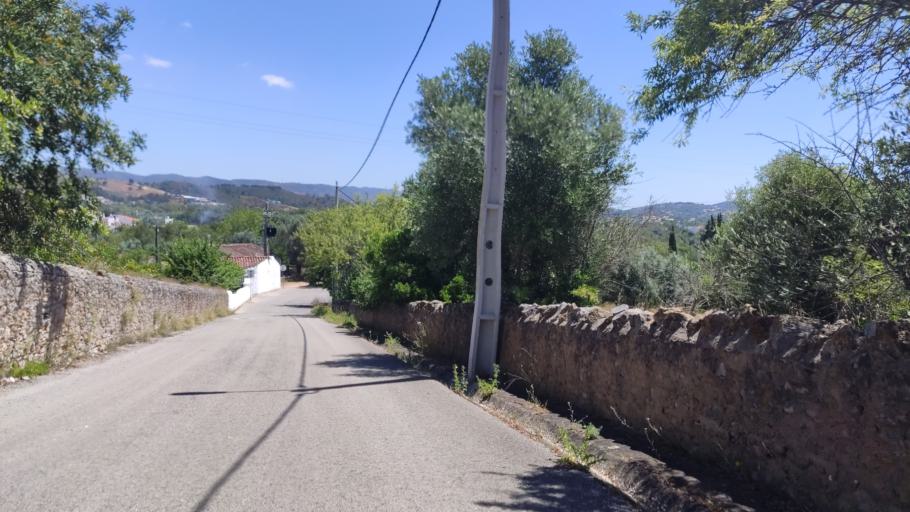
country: PT
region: Faro
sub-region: Sao Bras de Alportel
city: Sao Bras de Alportel
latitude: 37.1697
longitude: -7.9110
